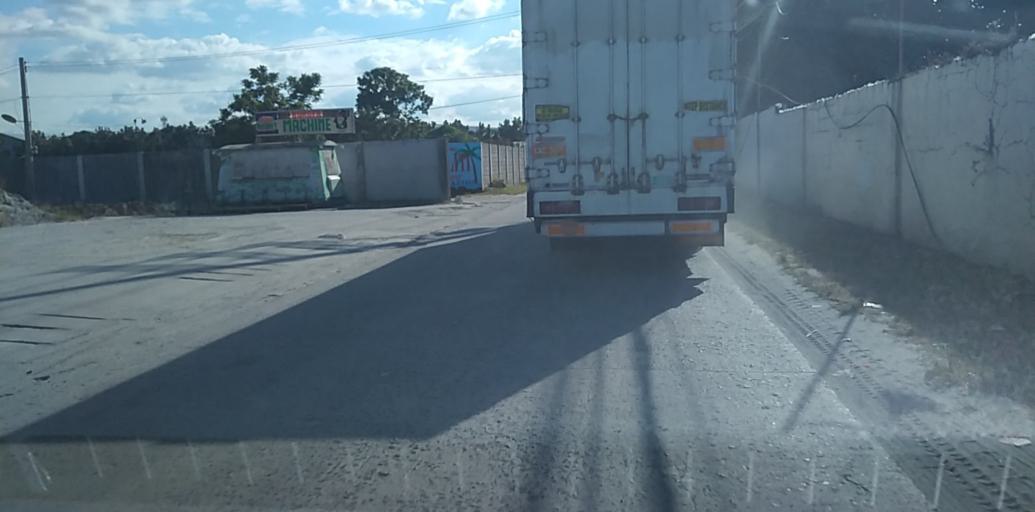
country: PH
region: Central Luzon
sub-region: Province of Pampanga
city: Telabastagan
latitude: 15.1080
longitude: 120.6265
